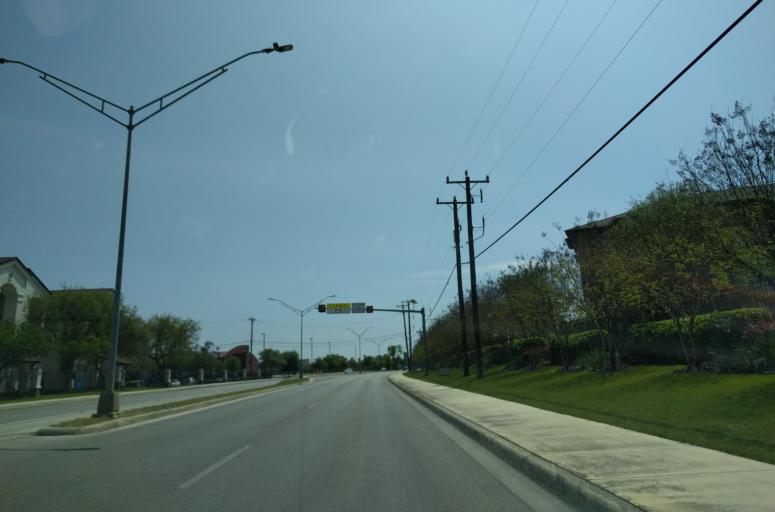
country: US
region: Texas
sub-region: Bexar County
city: Shavano Park
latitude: 29.5777
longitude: -98.5867
